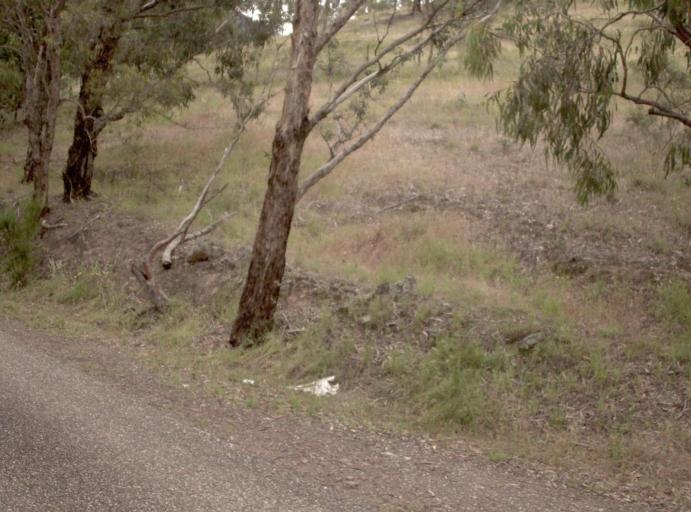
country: AU
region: Victoria
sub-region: East Gippsland
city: Bairnsdale
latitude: -37.5083
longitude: 147.2024
